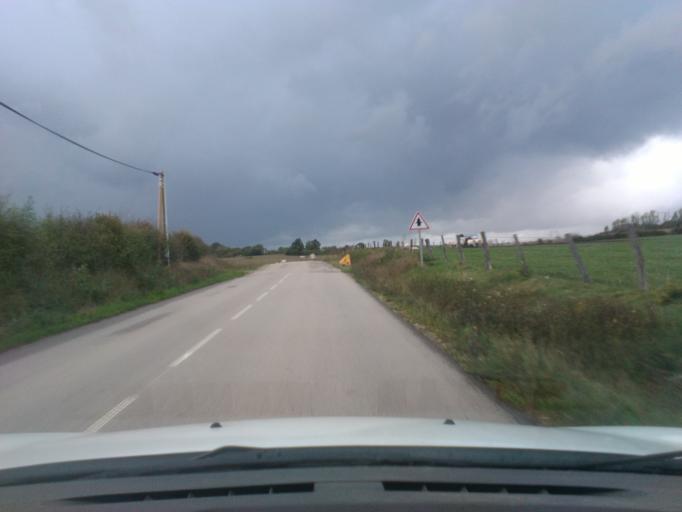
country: FR
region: Lorraine
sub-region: Departement des Vosges
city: Deyvillers
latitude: 48.2632
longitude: 6.5224
